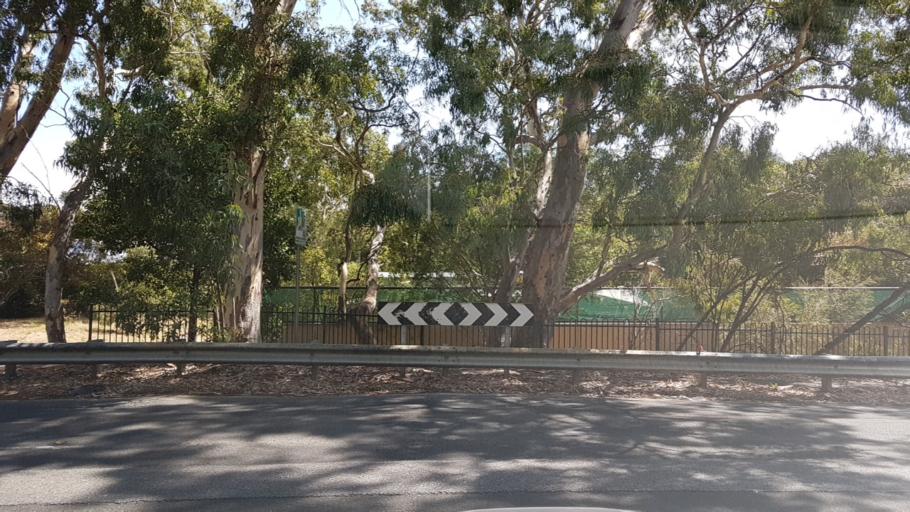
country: AU
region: South Australia
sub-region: Mitcham
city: Belair
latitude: -35.0078
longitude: 138.6333
